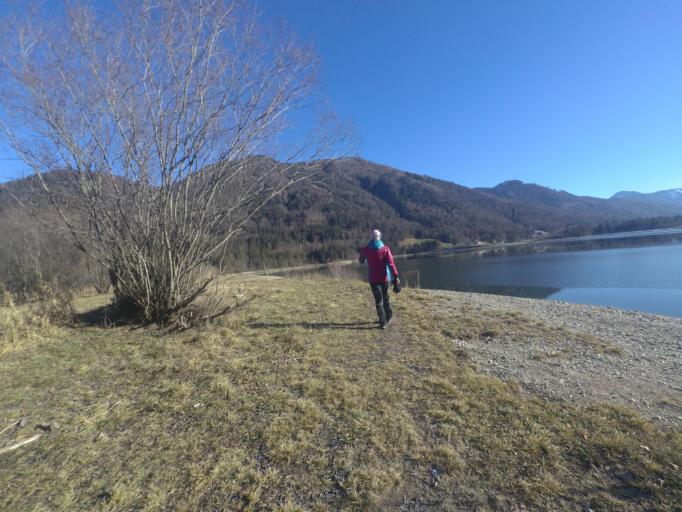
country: AT
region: Salzburg
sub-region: Politischer Bezirk Salzburg-Umgebung
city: Faistenau
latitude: 47.7518
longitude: 13.2428
